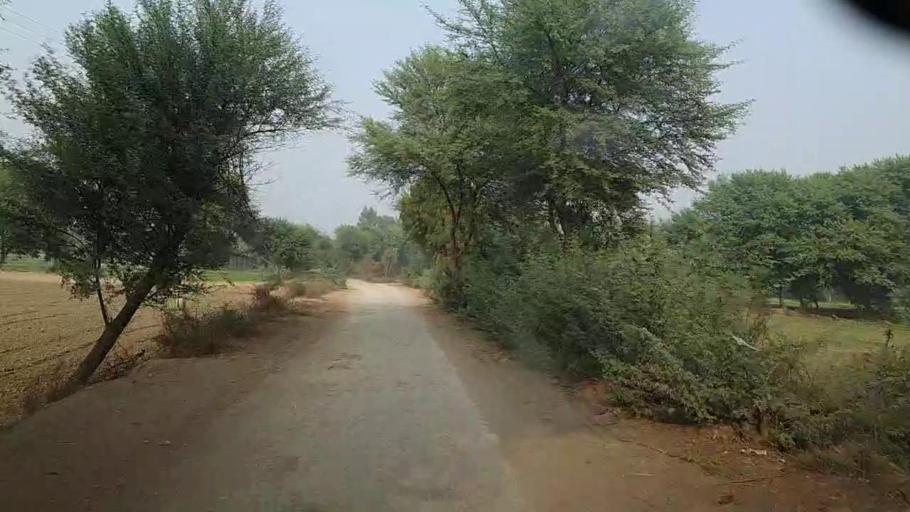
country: PK
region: Sindh
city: Bozdar
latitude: 27.1461
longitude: 68.6692
